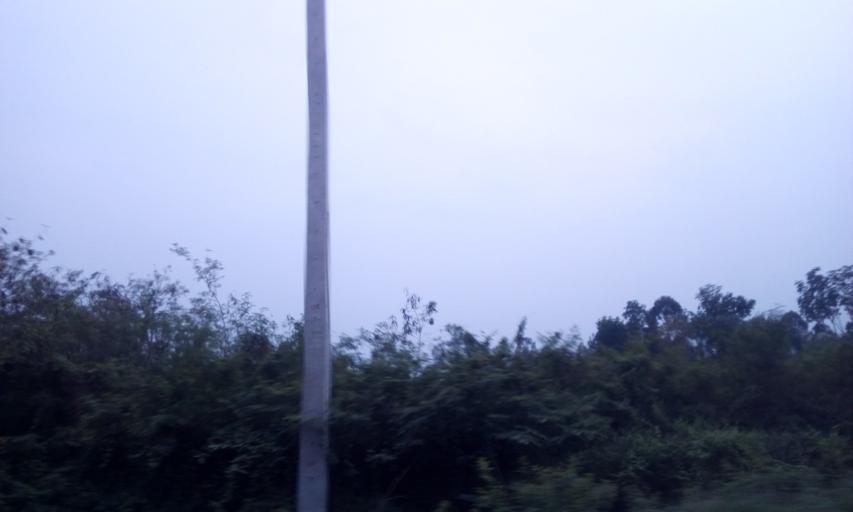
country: TH
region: Chachoengsao
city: Plaeng Yao
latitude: 13.5756
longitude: 101.2537
